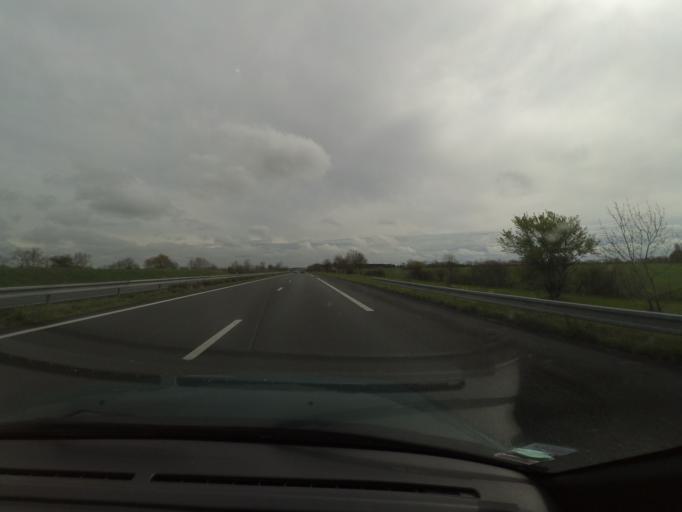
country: FR
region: Pays de la Loire
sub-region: Departement de Maine-et-Loire
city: Ingrandes
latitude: 47.4183
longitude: -0.9696
